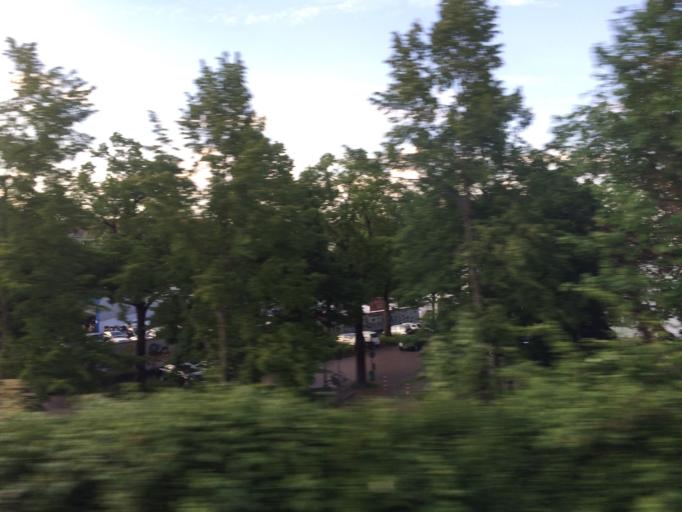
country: DE
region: North Rhine-Westphalia
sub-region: Regierungsbezirk Dusseldorf
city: Dusseldorf
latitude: 51.2086
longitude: 6.7998
